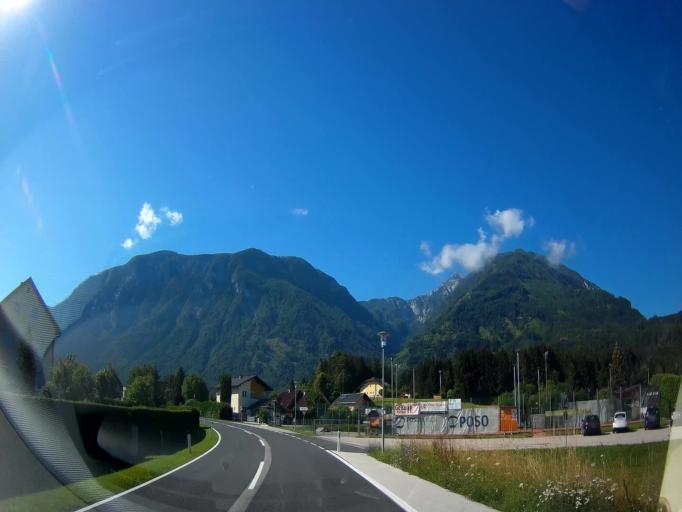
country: AT
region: Carinthia
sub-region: Politischer Bezirk Volkermarkt
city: Gallizien
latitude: 46.5532
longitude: 14.5115
